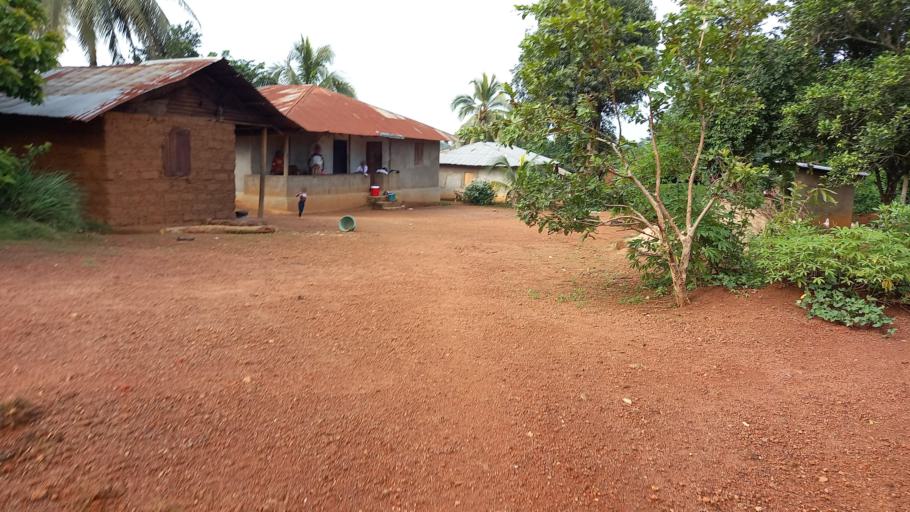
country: SL
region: Eastern Province
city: Kailahun
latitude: 8.2689
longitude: -10.5806
